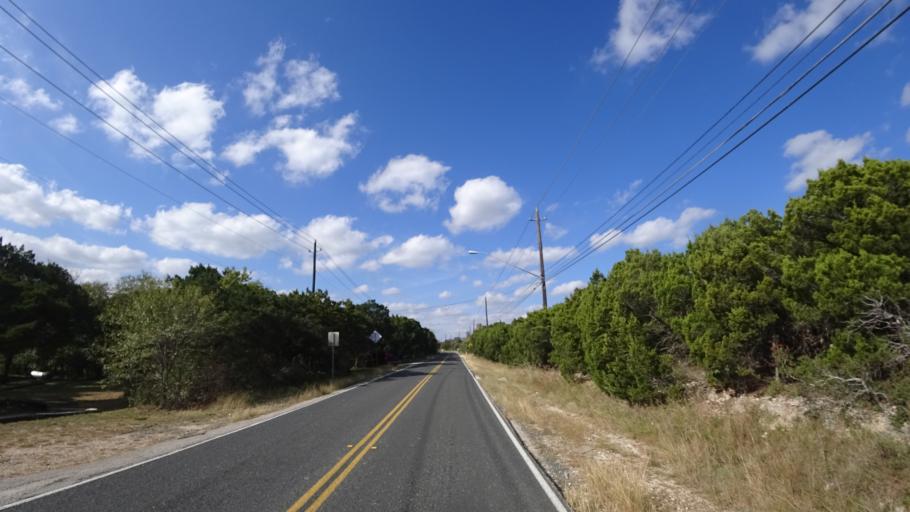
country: US
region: Texas
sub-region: Travis County
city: Barton Creek
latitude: 30.2427
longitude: -97.8787
